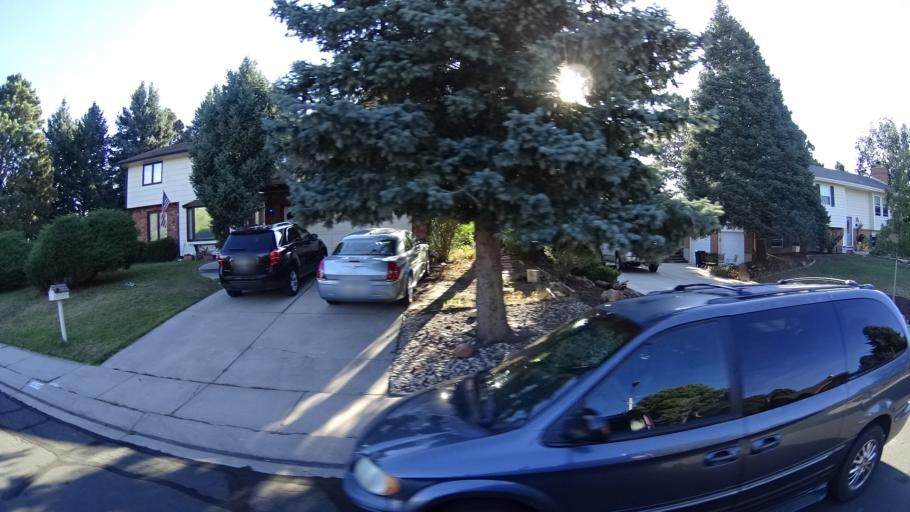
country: US
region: Colorado
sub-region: El Paso County
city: Cimarron Hills
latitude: 38.8831
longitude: -104.7653
